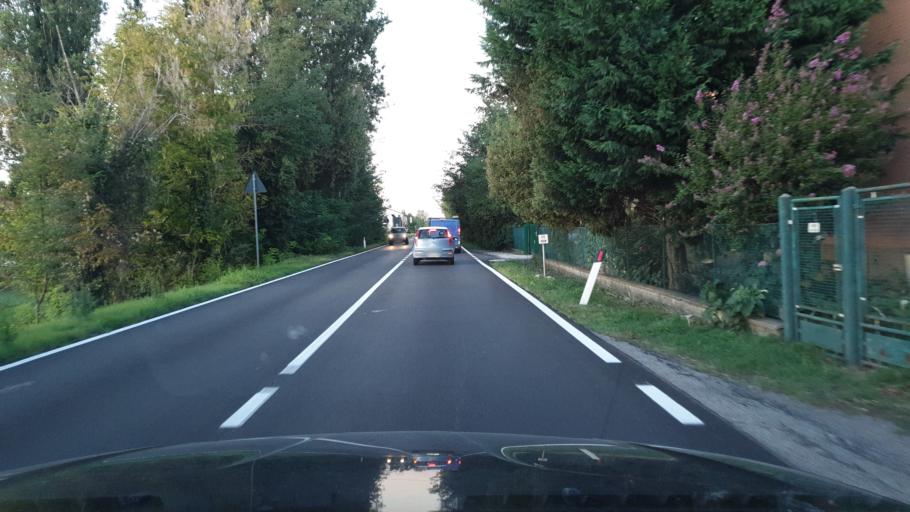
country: IT
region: Emilia-Romagna
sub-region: Provincia di Bologna
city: Ca De Fabbri
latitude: 44.6007
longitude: 11.4395
